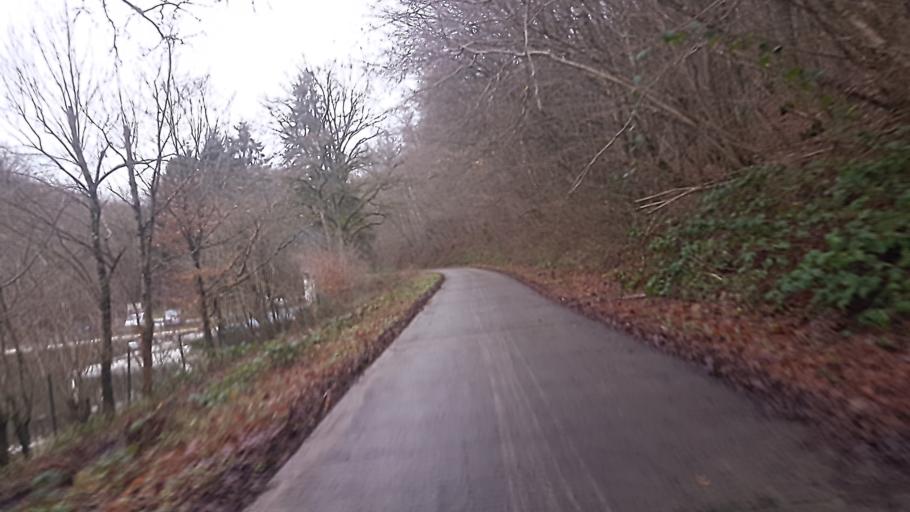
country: BE
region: Wallonia
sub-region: Province de Namur
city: Couvin
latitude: 50.0602
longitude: 4.5992
